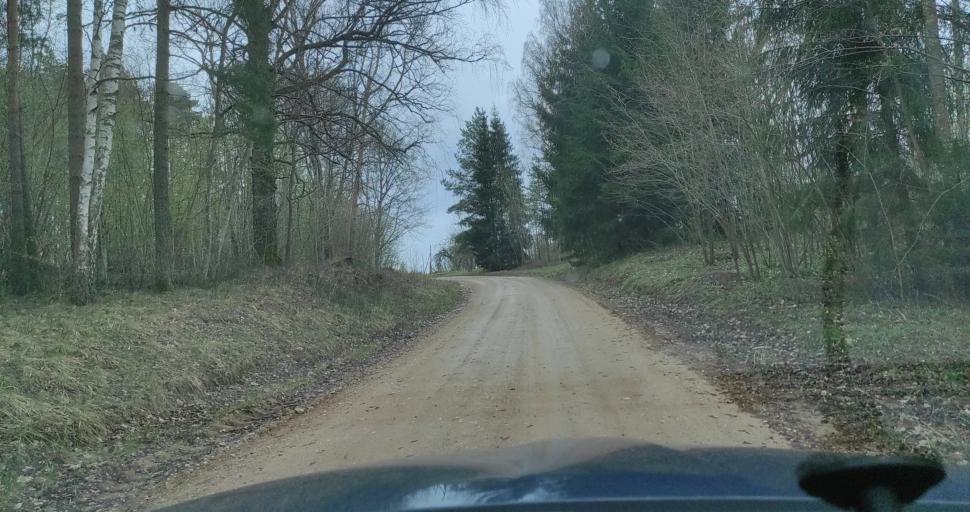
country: LV
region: Kuldigas Rajons
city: Kuldiga
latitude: 57.0573
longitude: 21.8076
